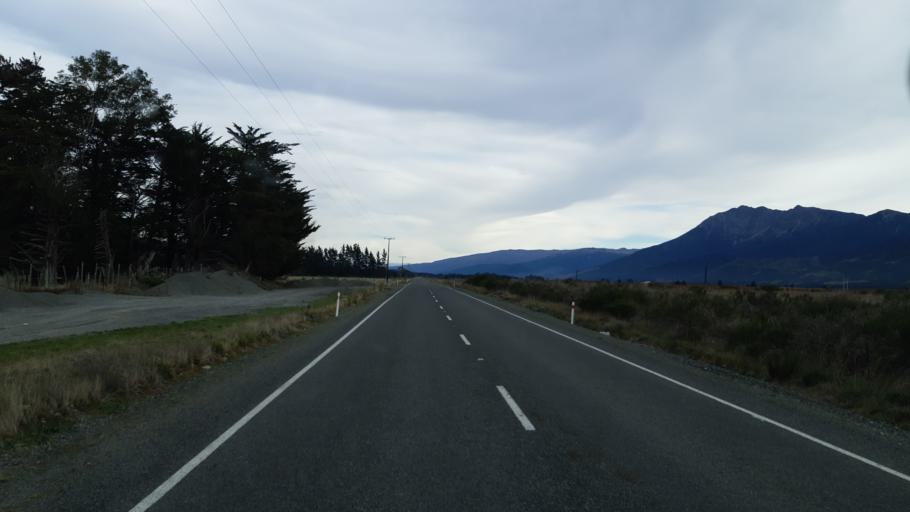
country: NZ
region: Tasman
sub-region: Tasman District
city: Richmond
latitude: -41.6176
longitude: 173.3750
